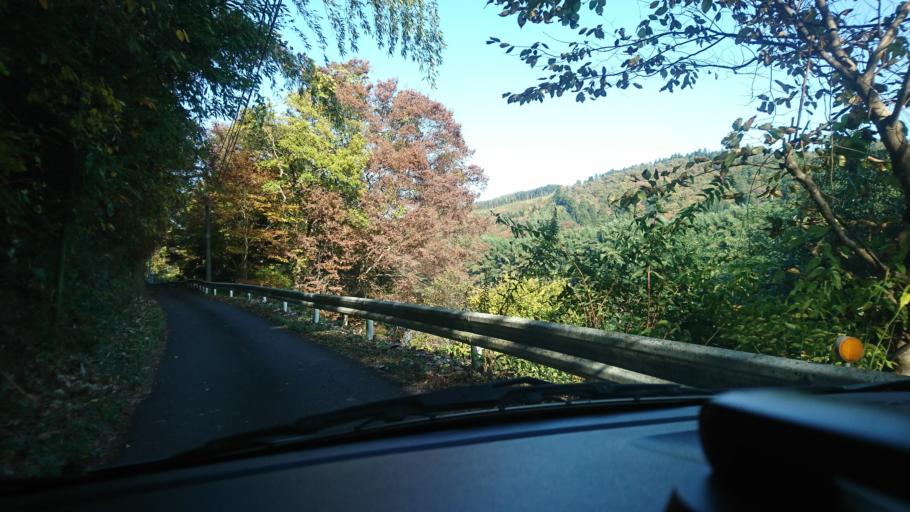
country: JP
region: Iwate
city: Ichinoseki
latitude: 38.7990
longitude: 141.2465
